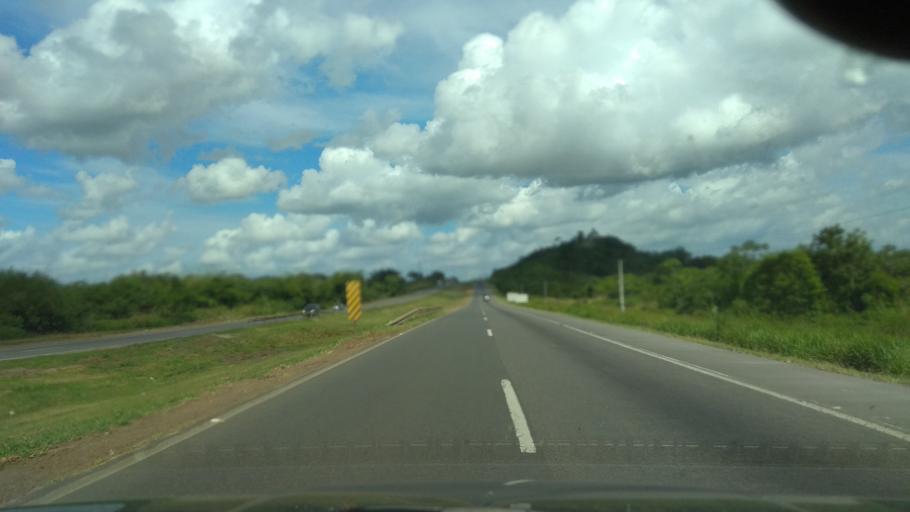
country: BR
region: Bahia
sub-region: Simoes Filho
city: Simoes Filho
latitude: -12.6642
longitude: -38.4707
